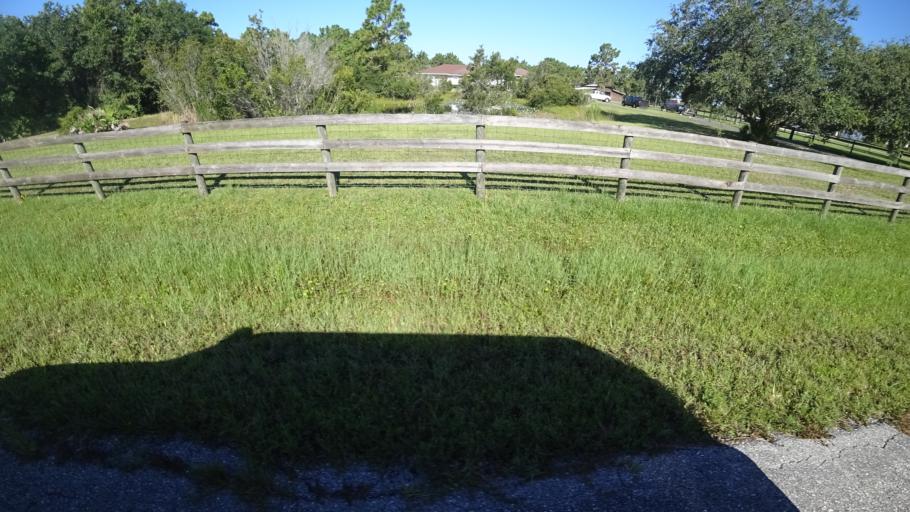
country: US
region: Florida
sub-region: Sarasota County
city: The Meadows
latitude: 27.4097
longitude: -82.3121
